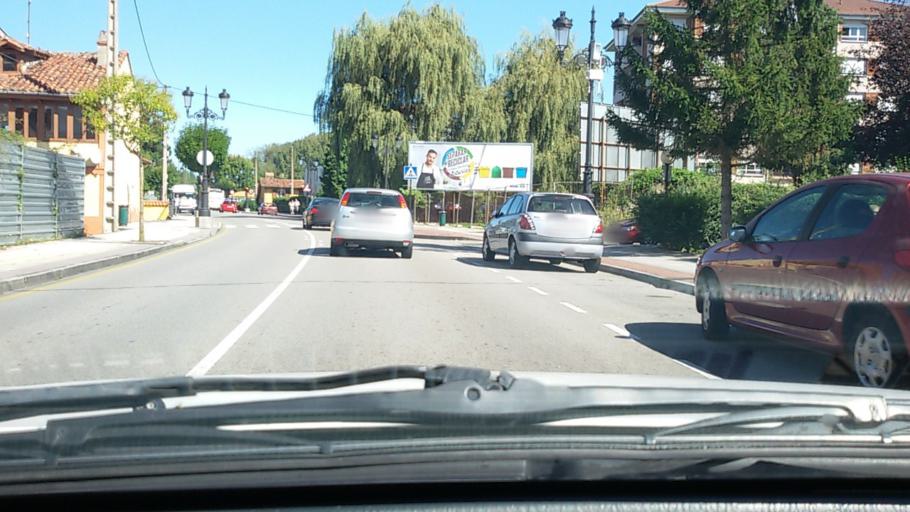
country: ES
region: Asturias
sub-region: Province of Asturias
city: Lugones
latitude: 43.3885
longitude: -5.8207
